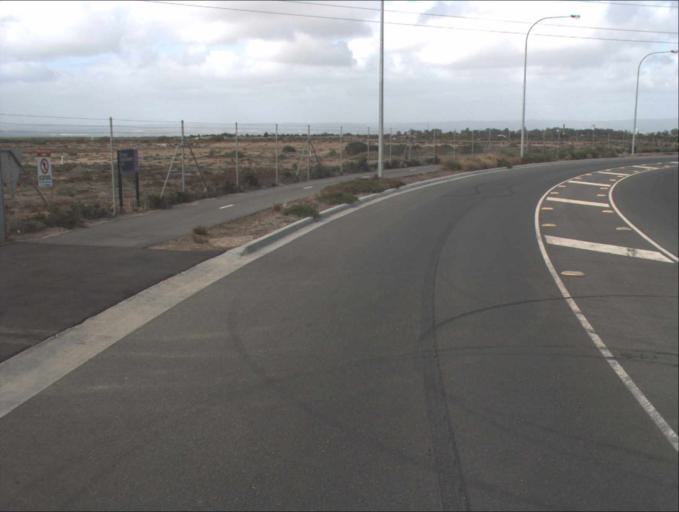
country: AU
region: South Australia
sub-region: Port Adelaide Enfield
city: Birkenhead
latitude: -34.7691
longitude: 138.5094
